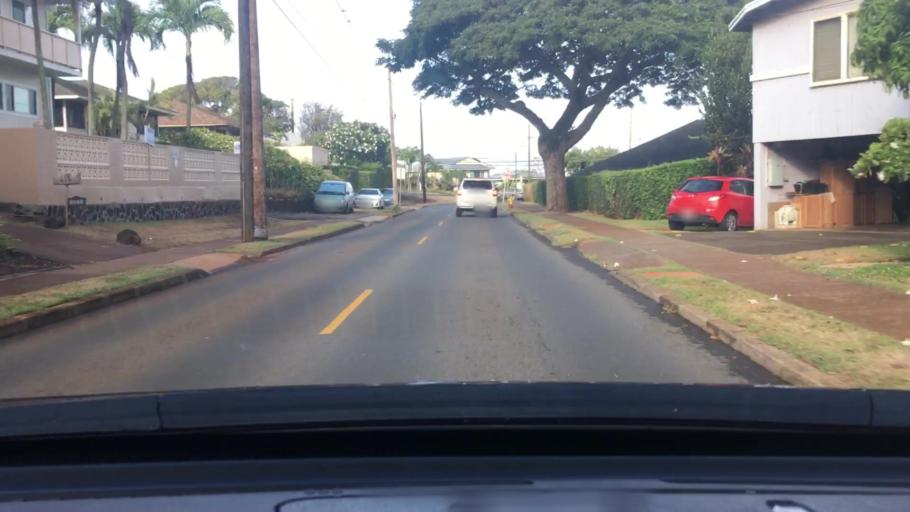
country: US
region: Hawaii
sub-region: Honolulu County
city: Honolulu
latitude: 21.2783
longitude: -157.8005
